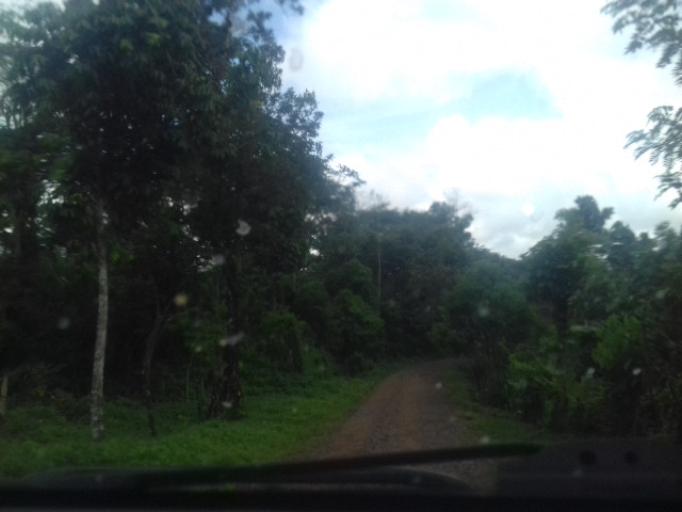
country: NI
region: Matagalpa
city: Matiguas
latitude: 12.9395
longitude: -85.3688
